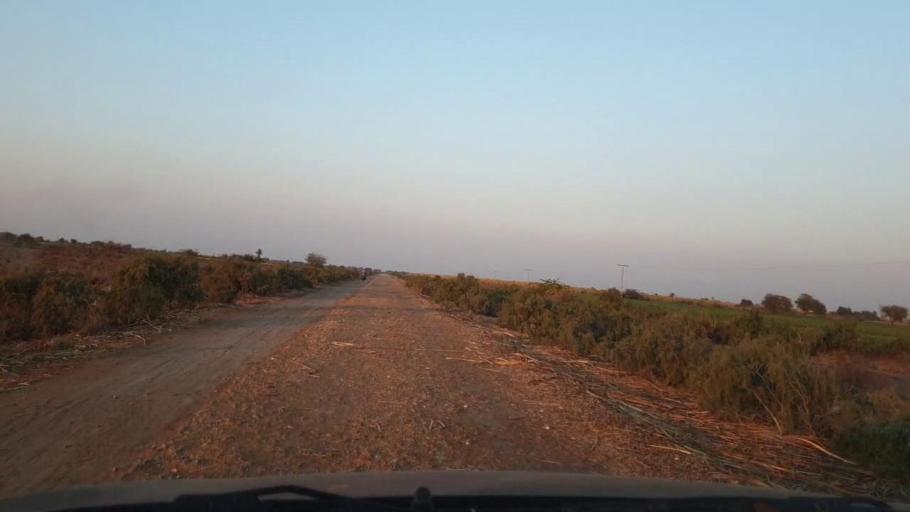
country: PK
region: Sindh
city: Jhol
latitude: 25.9237
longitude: 68.9644
